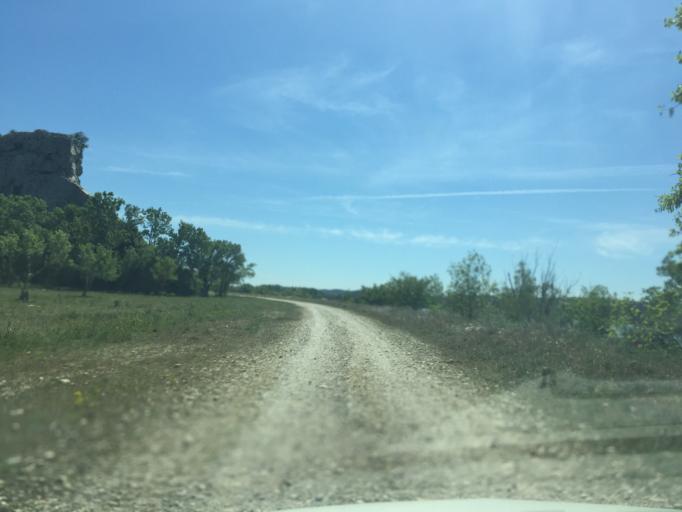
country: FR
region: Languedoc-Roussillon
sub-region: Departement du Gard
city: Roquemaure
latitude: 44.0551
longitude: 4.7902
